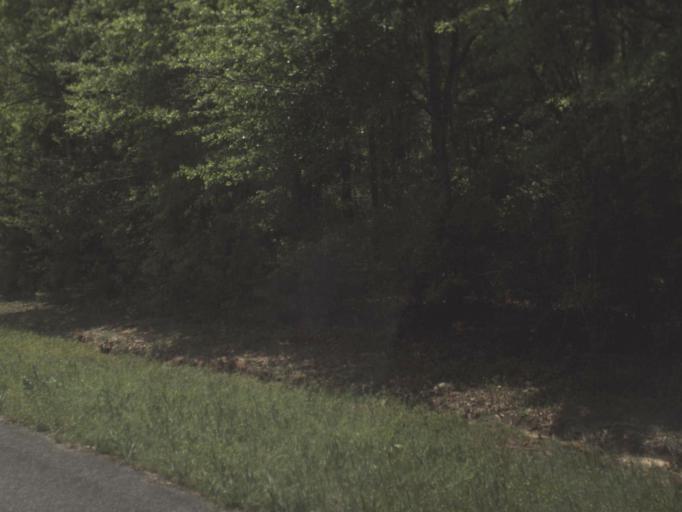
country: US
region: Florida
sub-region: Okaloosa County
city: Crestview
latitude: 30.9622
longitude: -86.6323
